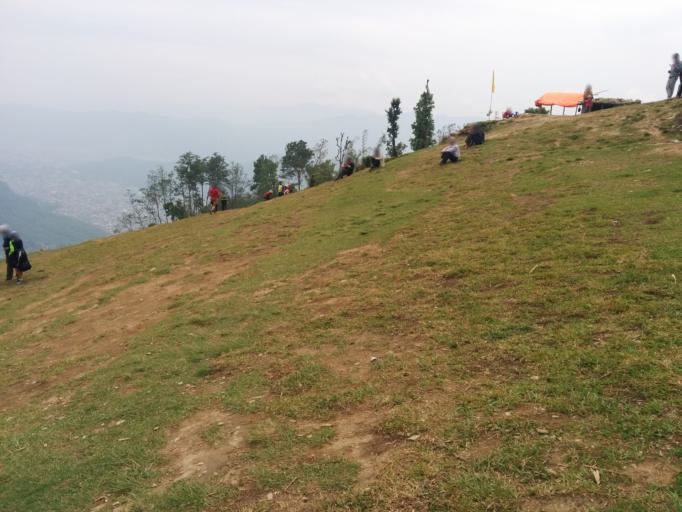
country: NP
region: Western Region
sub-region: Gandaki Zone
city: Pokhara
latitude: 28.2438
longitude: 83.9513
